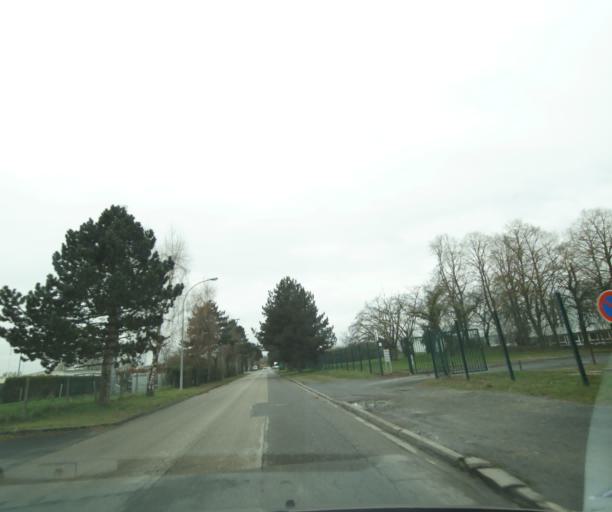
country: FR
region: Picardie
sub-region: Departement de l'Oise
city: Noyon
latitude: 49.5757
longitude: 3.0211
